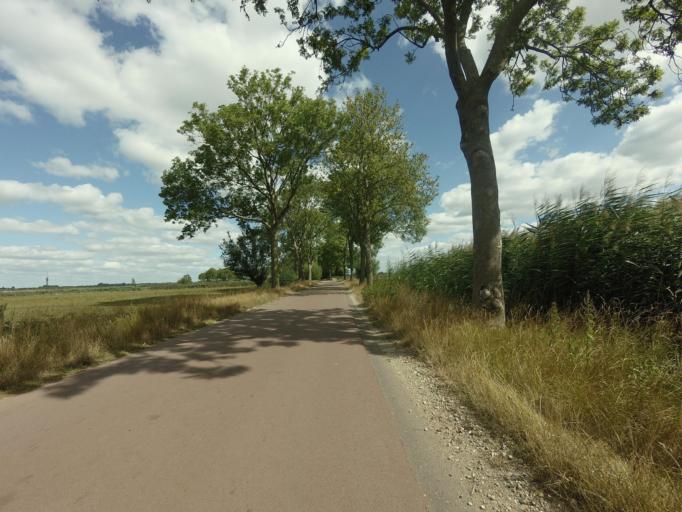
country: NL
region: North Brabant
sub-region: Gemeente Oss
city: Berghem
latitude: 51.7840
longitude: 5.5999
